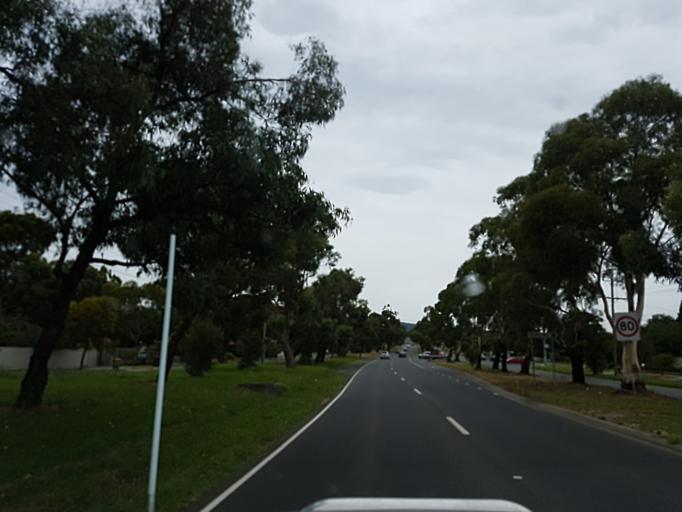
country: AU
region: Victoria
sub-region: Knox
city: Bayswater
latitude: -37.8557
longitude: 145.2525
